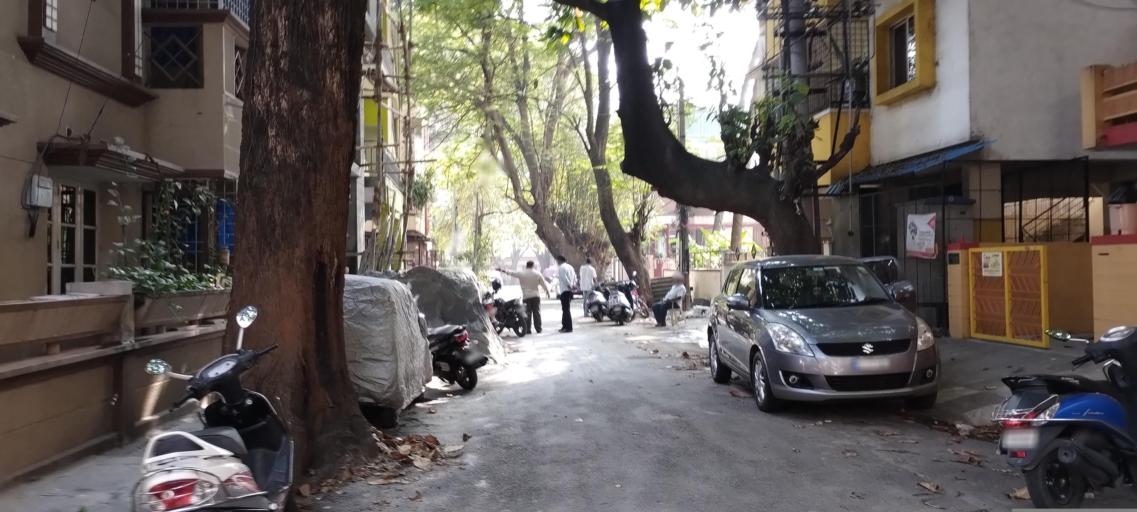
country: IN
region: Karnataka
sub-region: Bangalore Urban
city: Bangalore
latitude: 12.9362
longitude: 77.5427
